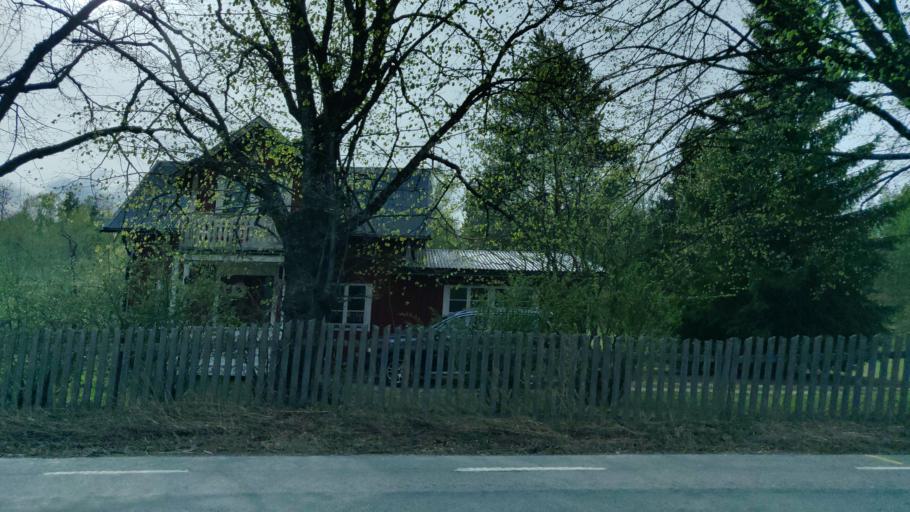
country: SE
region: Vaermland
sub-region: Munkfors Kommun
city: Munkfors
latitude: 59.8074
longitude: 13.5066
